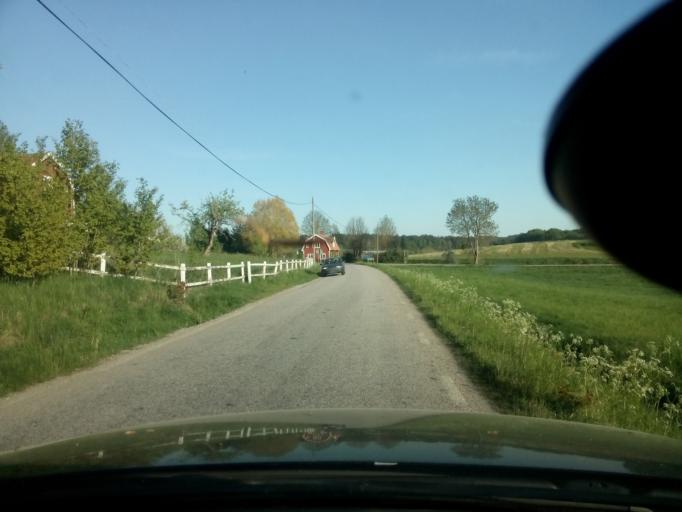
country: SE
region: Soedermanland
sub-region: Nykopings Kommun
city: Nykoping
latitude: 58.8692
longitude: 17.0133
